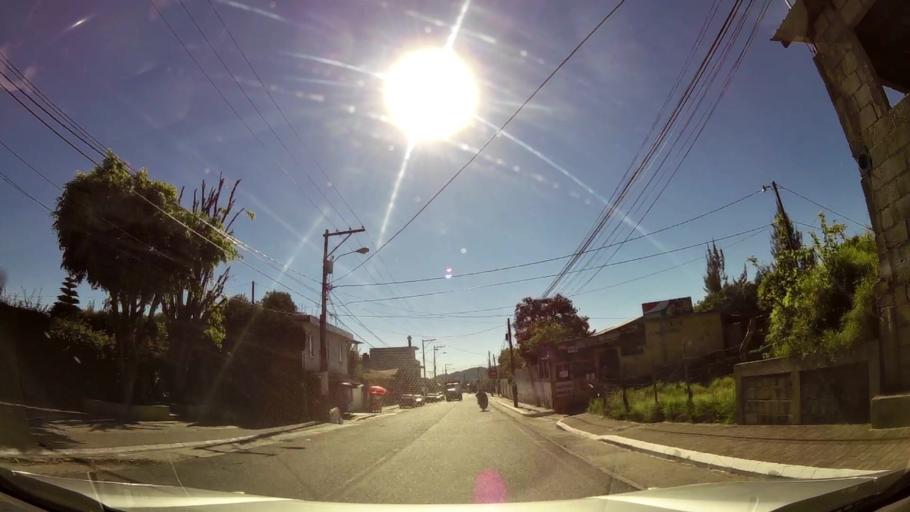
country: GT
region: Guatemala
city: Fraijanes
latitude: 14.4720
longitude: -90.4477
